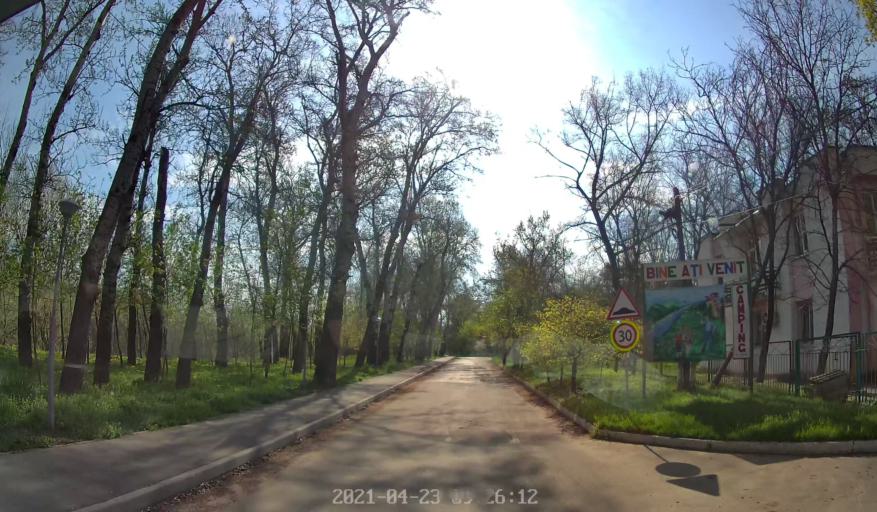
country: MD
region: Chisinau
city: Vadul lui Voda
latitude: 47.0873
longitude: 29.0930
